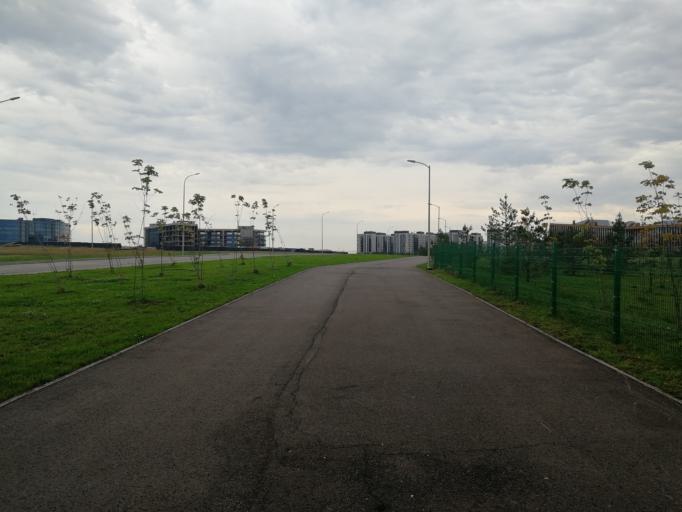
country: RU
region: Tatarstan
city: Sviyazhsk
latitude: 55.7566
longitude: 48.7460
